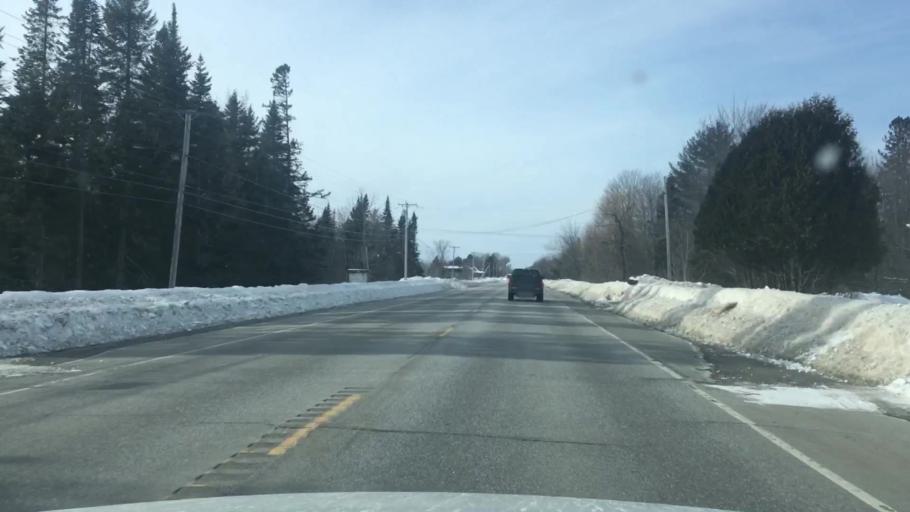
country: US
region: Maine
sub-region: Penobscot County
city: Kenduskeag
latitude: 44.9784
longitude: -68.9920
